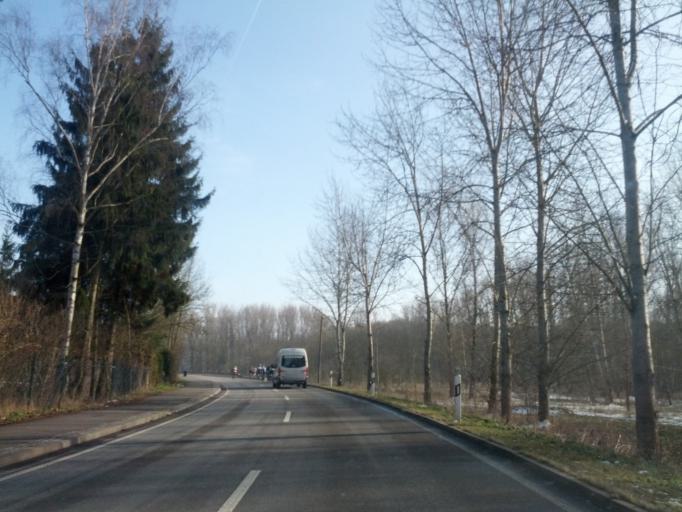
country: DE
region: Thuringia
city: Ingersleben
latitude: 50.9221
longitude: 10.9551
